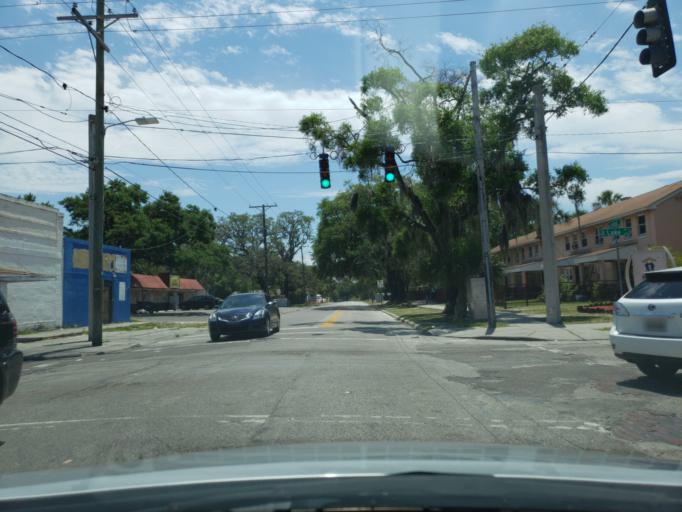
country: US
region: Florida
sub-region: Hillsborough County
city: Tampa
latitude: 27.9779
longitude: -82.4553
